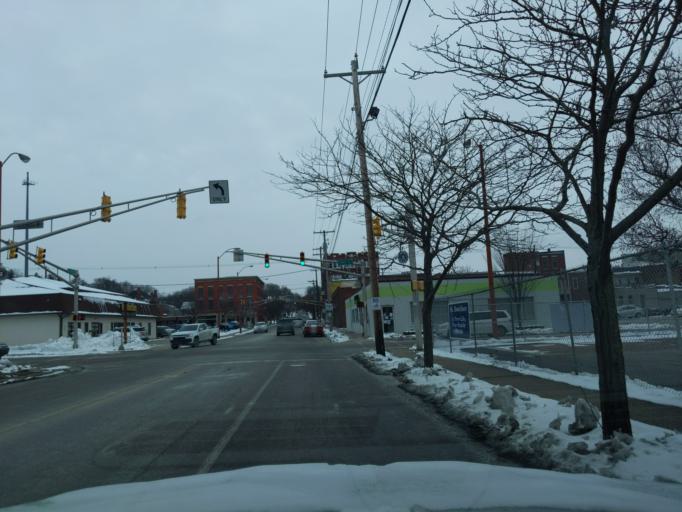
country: US
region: Indiana
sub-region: Tippecanoe County
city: Lafayette
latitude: 40.4203
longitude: -86.8869
